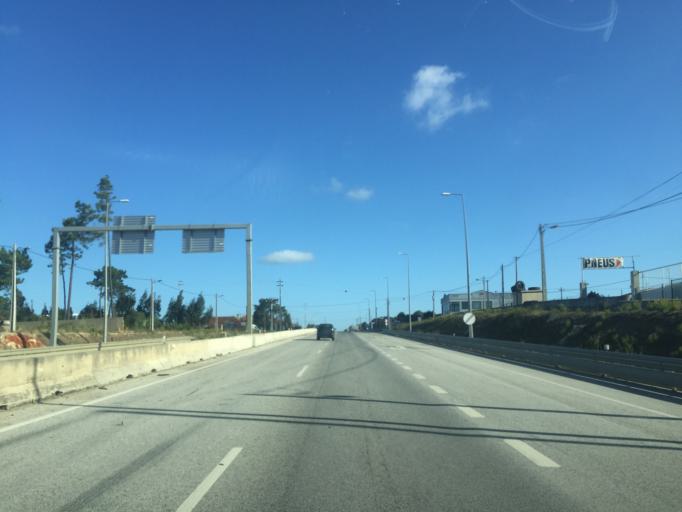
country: PT
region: Leiria
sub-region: Alcobaca
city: Aljubarrota
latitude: 39.5585
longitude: -8.8866
